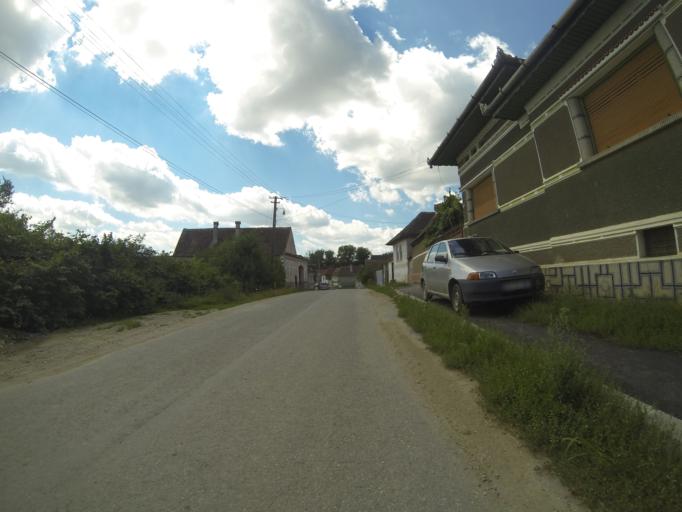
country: RO
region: Brasov
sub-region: Comuna Mandra
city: Mandra
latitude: 45.8458
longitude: 25.0349
